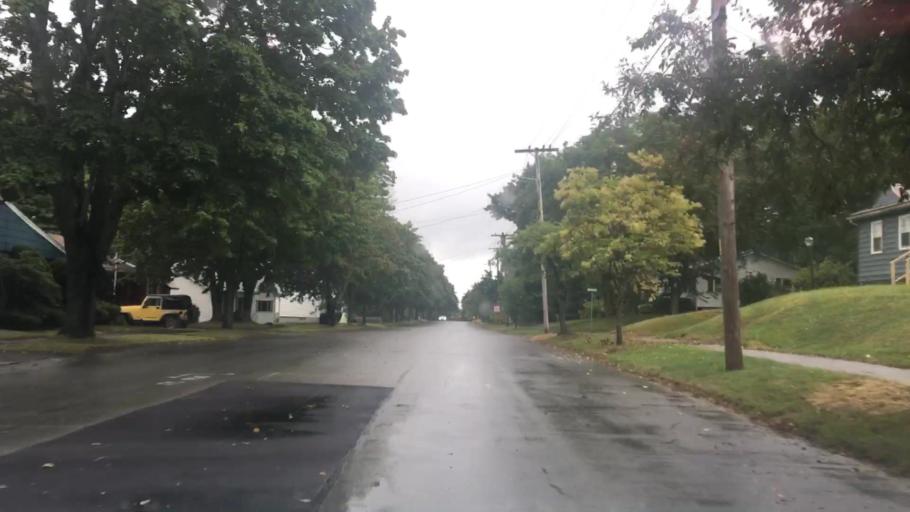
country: US
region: Maine
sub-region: Penobscot County
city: Brewer
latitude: 44.8174
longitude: -68.7605
